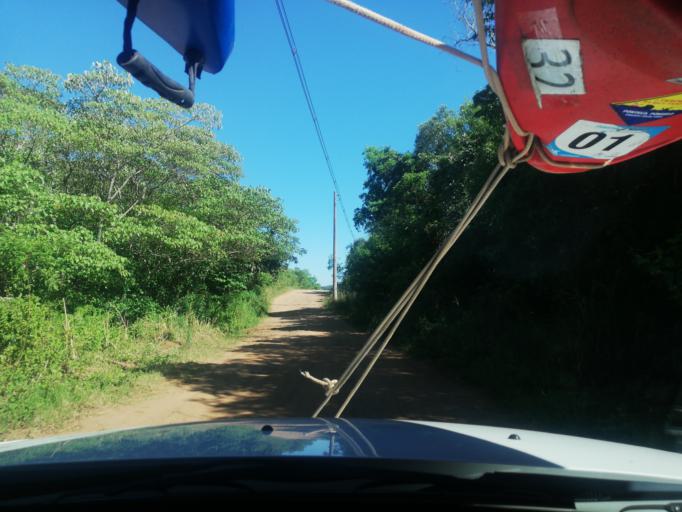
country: AR
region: Misiones
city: Santa Ana
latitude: -27.3345
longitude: -55.5826
